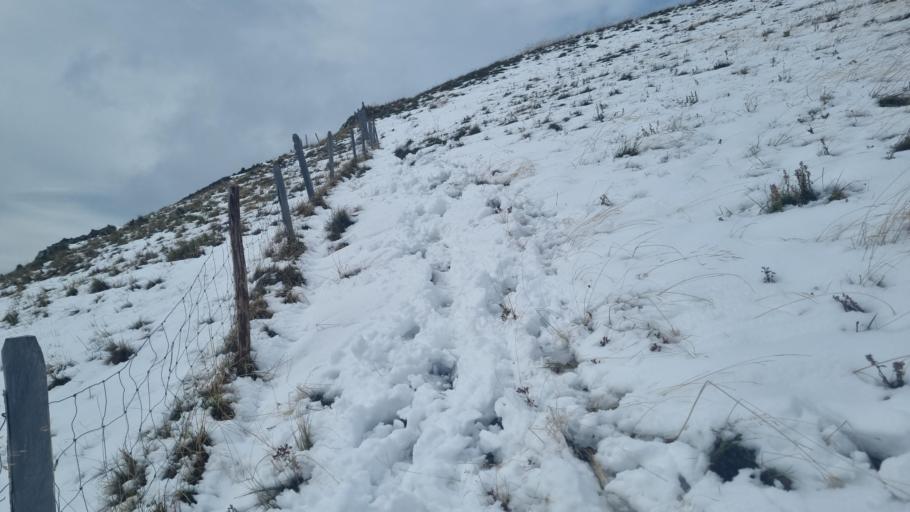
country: CH
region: Schwyz
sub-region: Bezirk March
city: Vorderthal
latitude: 47.1000
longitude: 8.9587
